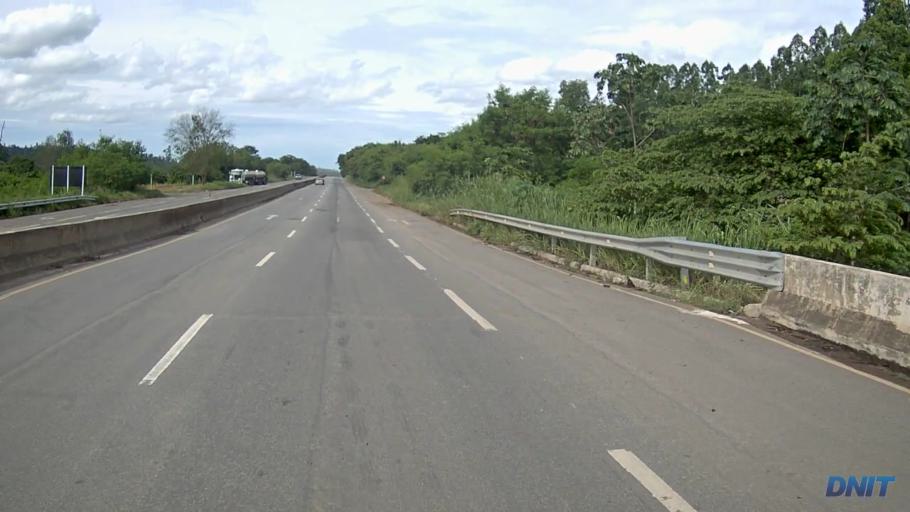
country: BR
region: Minas Gerais
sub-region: Ipaba
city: Ipaba
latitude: -19.3223
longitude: -42.4072
